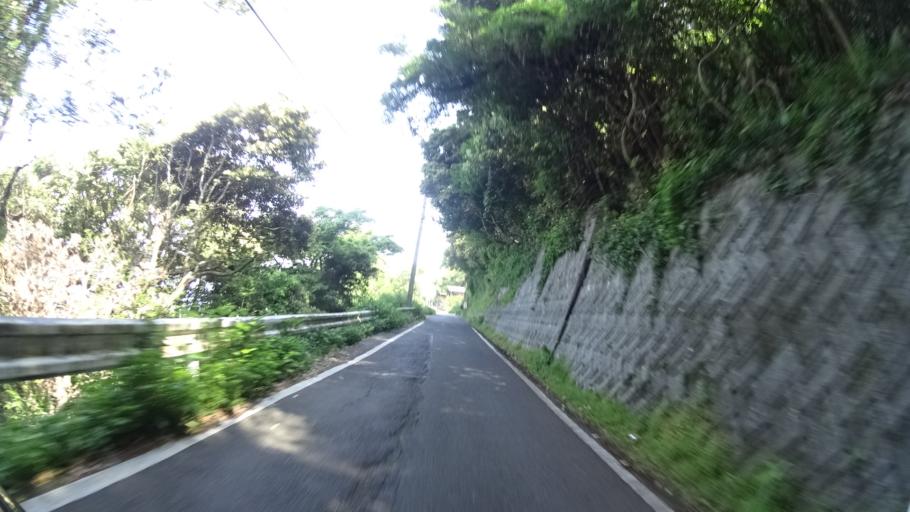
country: JP
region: Oita
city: Tsukumiura
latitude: 33.3518
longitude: 132.0301
